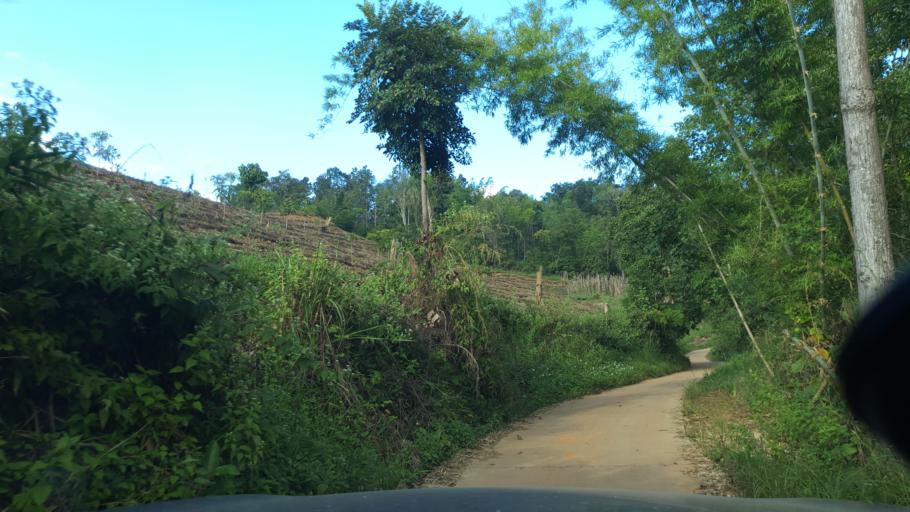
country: TH
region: Chiang Mai
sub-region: Amphoe Chiang Dao
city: Chiang Dao
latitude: 19.4065
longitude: 98.8325
